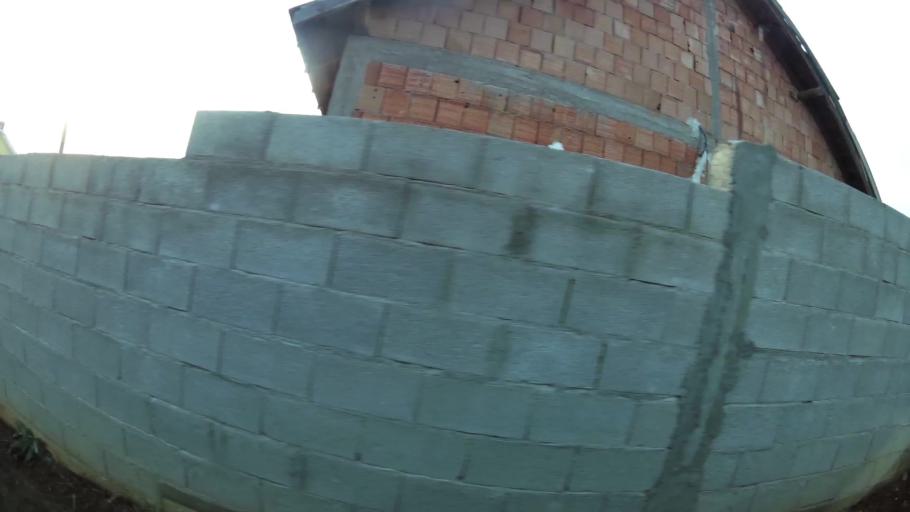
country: MK
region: Aracinovo
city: Arachinovo
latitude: 42.0224
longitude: 21.5730
